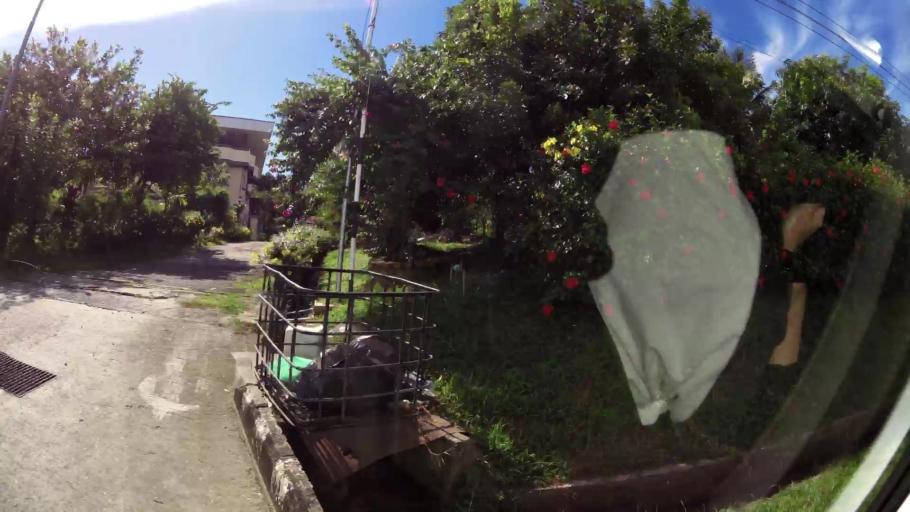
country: BN
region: Brunei and Muara
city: Bandar Seri Begawan
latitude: 5.0253
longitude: 115.0448
